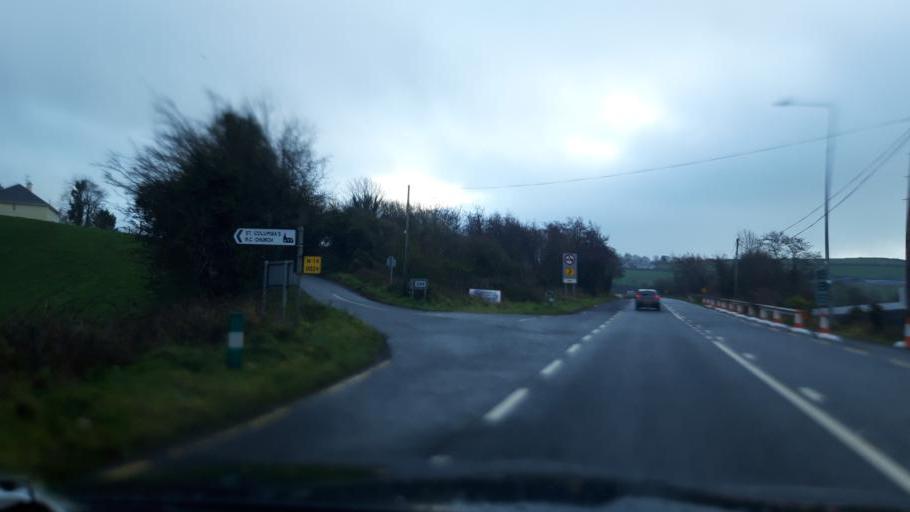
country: IE
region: Ulster
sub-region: County Donegal
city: Raphoe
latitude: 54.9383
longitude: -7.6160
